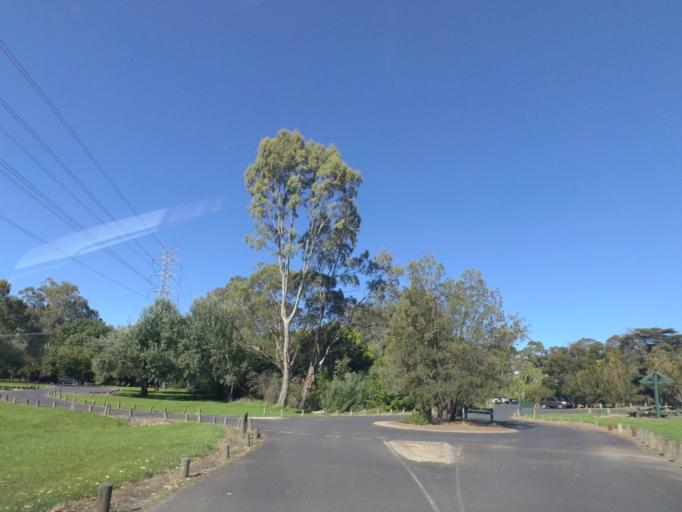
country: AU
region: Victoria
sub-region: Manningham
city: Bulleen
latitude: -37.7585
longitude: 145.0809
